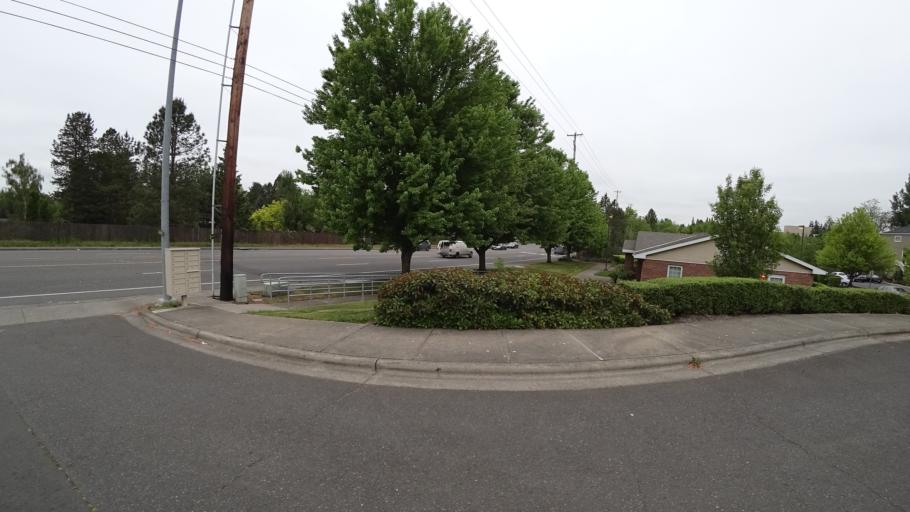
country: US
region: Oregon
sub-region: Washington County
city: Rockcreek
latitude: 45.5467
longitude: -122.8672
